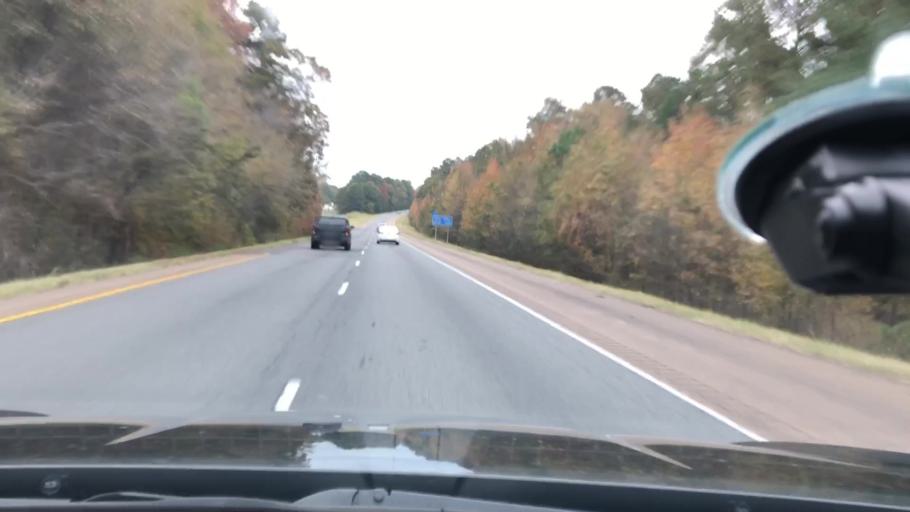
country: US
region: Arkansas
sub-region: Clark County
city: Gurdon
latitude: 33.9239
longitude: -93.2684
